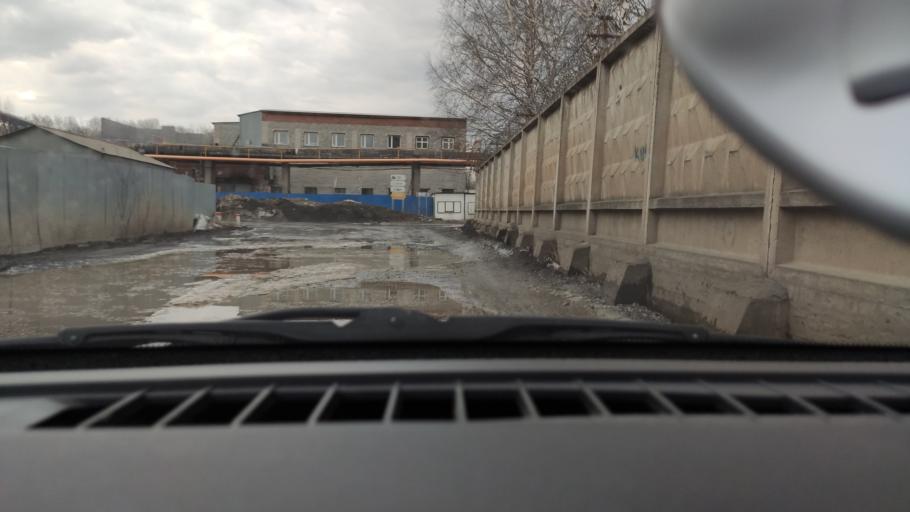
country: RU
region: Perm
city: Perm
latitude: 58.0424
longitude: 56.3106
